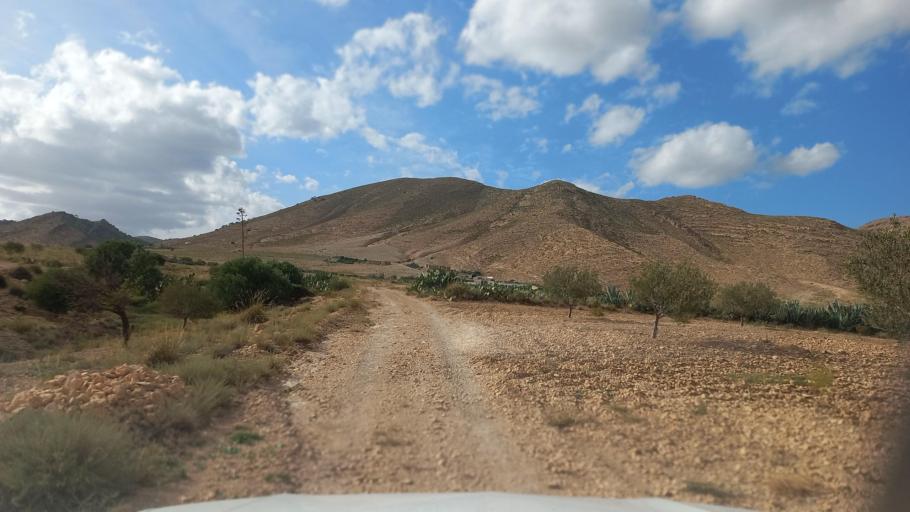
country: TN
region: Al Qasrayn
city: Sbiba
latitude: 35.4549
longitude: 9.0718
